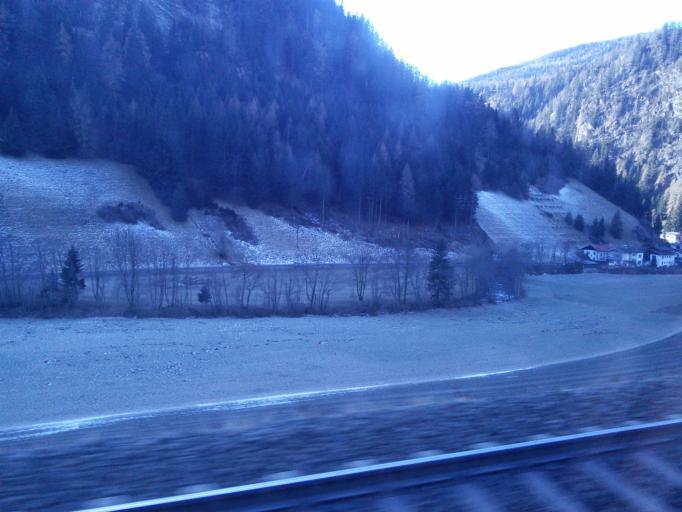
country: AT
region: Tyrol
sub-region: Politischer Bezirk Innsbruck Land
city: Gries am Brenner
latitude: 47.0640
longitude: 11.4935
